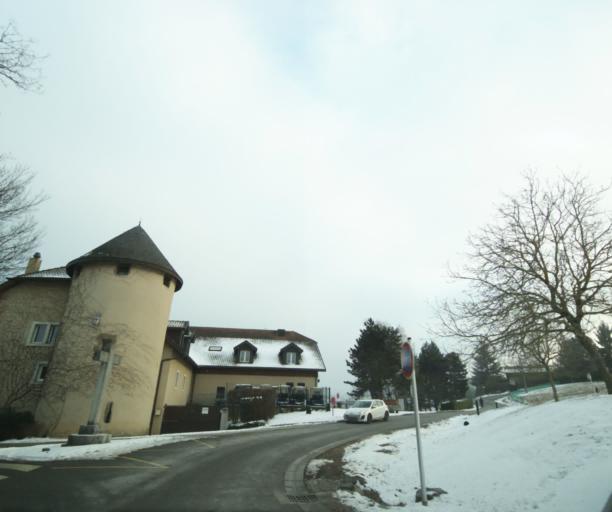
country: FR
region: Rhone-Alpes
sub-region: Departement de la Haute-Savoie
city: Reignier-Esery
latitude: 46.1429
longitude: 6.2385
